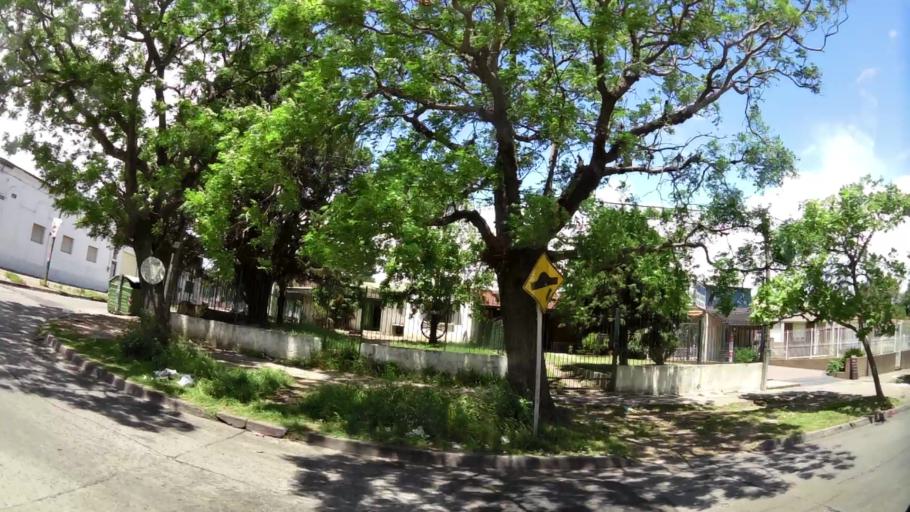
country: UY
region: Montevideo
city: Montevideo
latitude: -34.8388
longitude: -56.1949
